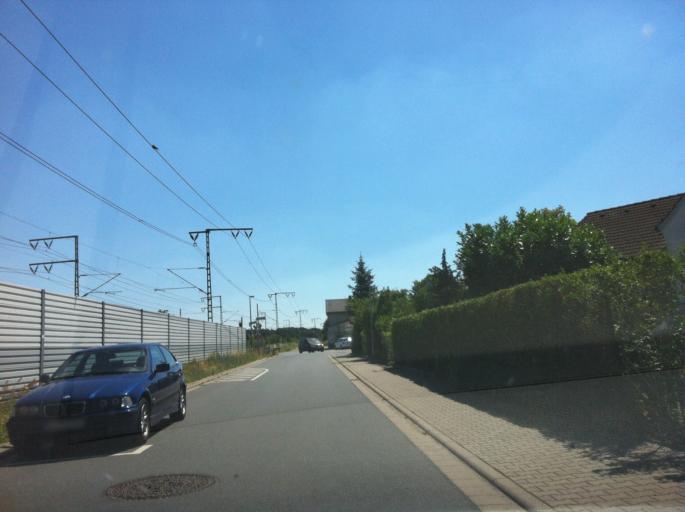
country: DE
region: Hesse
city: Weiterstadt
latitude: 49.9071
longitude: 8.5934
